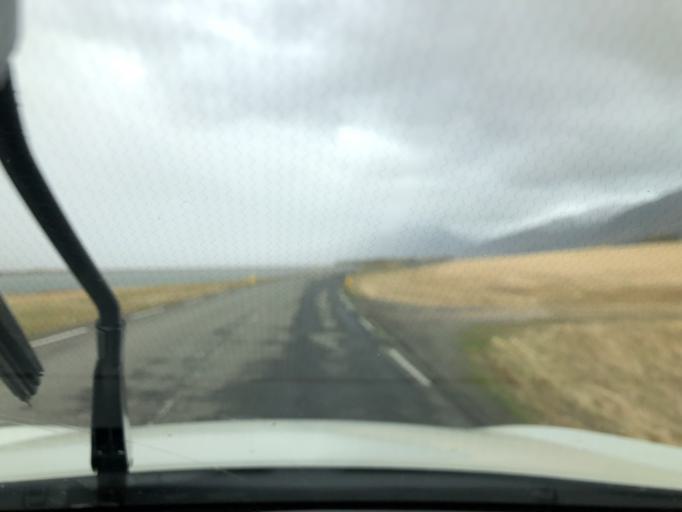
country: IS
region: East
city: Hoefn
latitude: 64.3310
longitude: -15.2424
